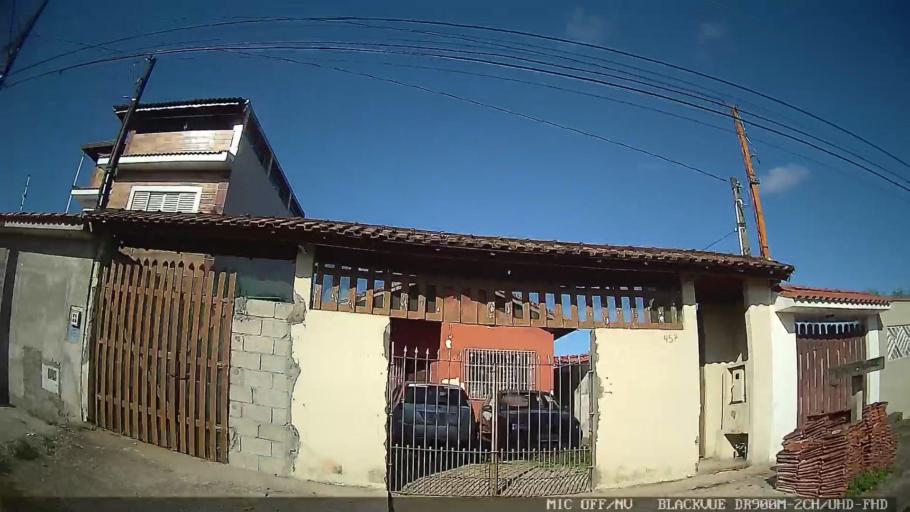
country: BR
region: Sao Paulo
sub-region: Peruibe
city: Peruibe
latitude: -24.2702
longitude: -46.9362
